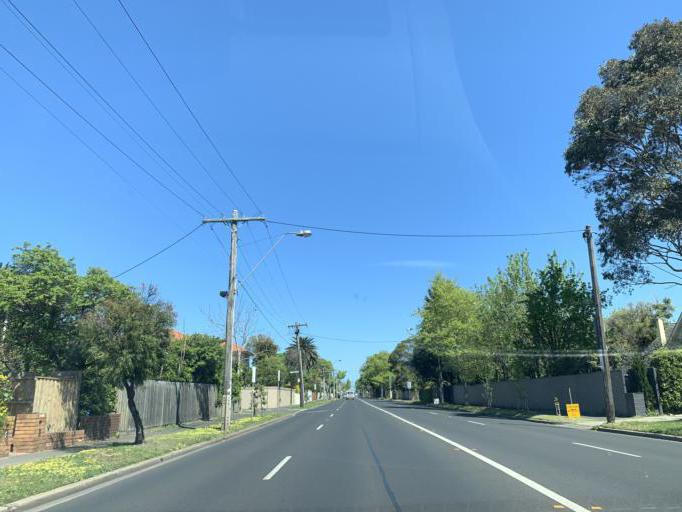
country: AU
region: Victoria
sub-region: Port Phillip
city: Elwood
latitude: -37.8983
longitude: 144.9895
